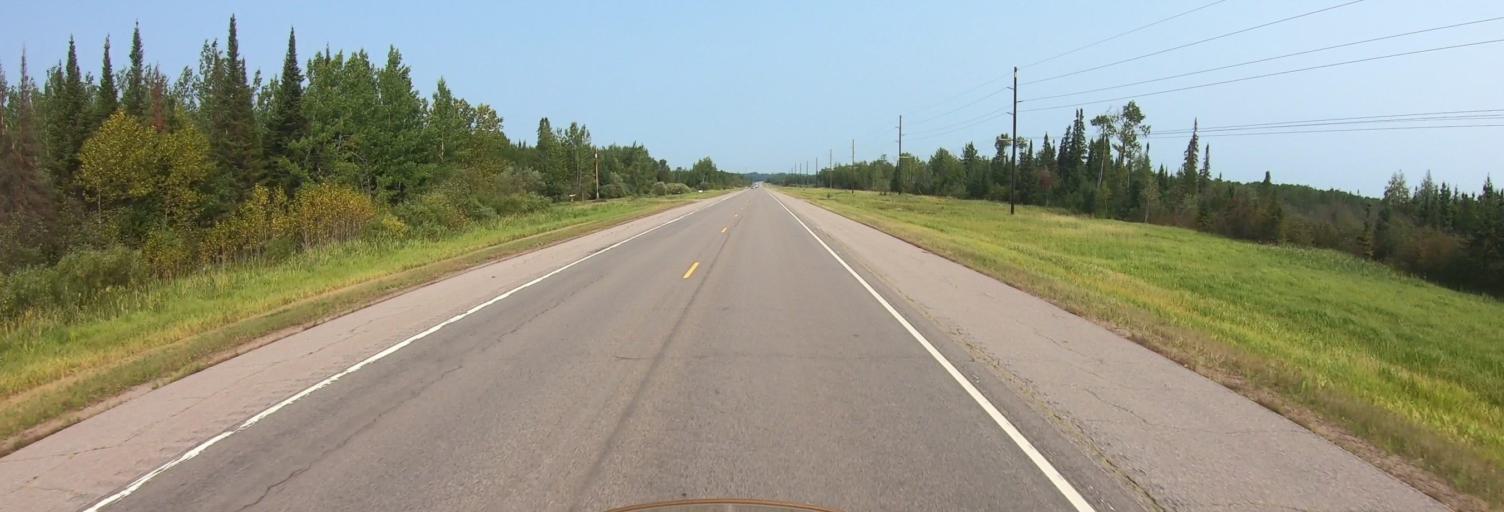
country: US
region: Minnesota
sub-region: Saint Louis County
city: Chisholm
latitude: 47.9335
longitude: -92.8287
